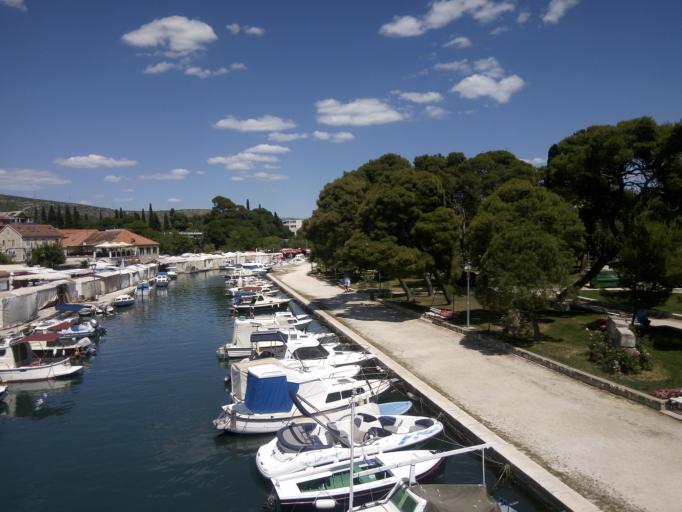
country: HR
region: Splitsko-Dalmatinska
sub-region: Grad Trogir
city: Trogir
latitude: 43.5173
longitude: 16.2480
